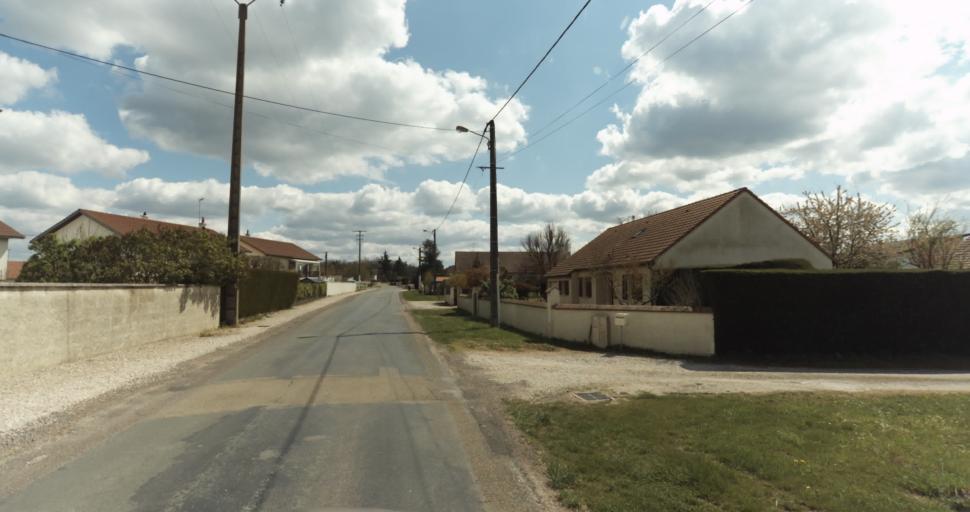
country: FR
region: Bourgogne
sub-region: Departement de la Cote-d'Or
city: Auxonne
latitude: 47.1871
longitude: 5.4041
